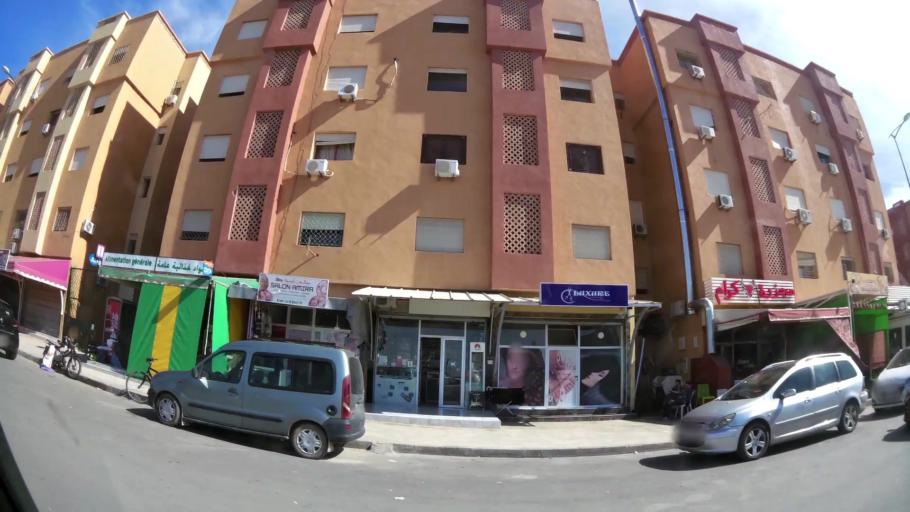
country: MA
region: Marrakech-Tensift-Al Haouz
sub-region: Marrakech
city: Marrakesh
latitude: 31.6604
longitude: -8.0222
